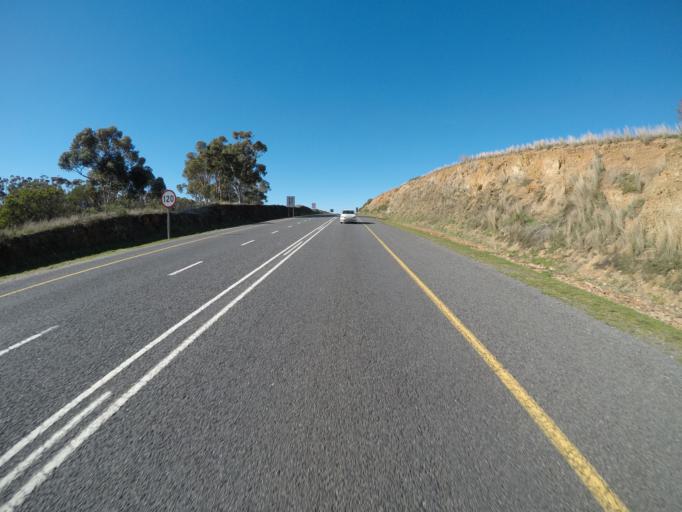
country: ZA
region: Western Cape
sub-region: Overberg District Municipality
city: Hermanus
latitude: -34.2352
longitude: 19.2202
